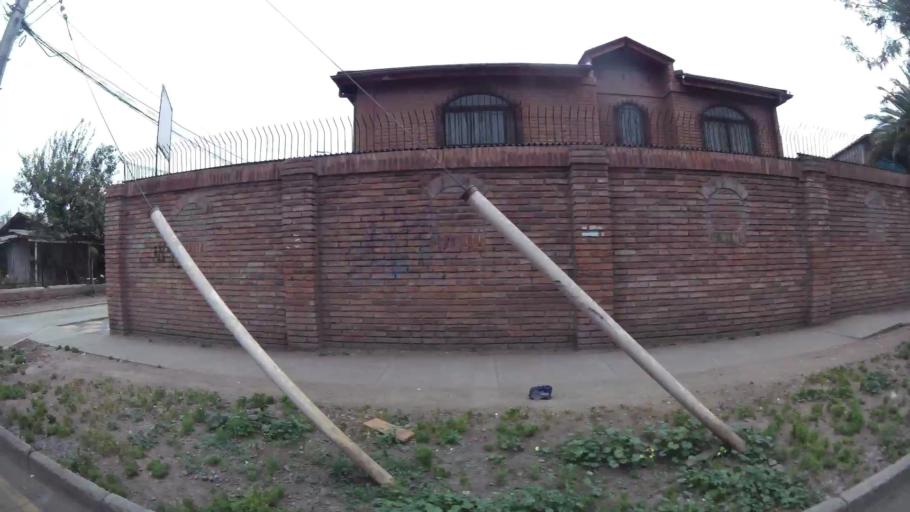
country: CL
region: Santiago Metropolitan
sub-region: Provincia de Chacabuco
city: Chicureo Abajo
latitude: -33.1938
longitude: -70.6753
